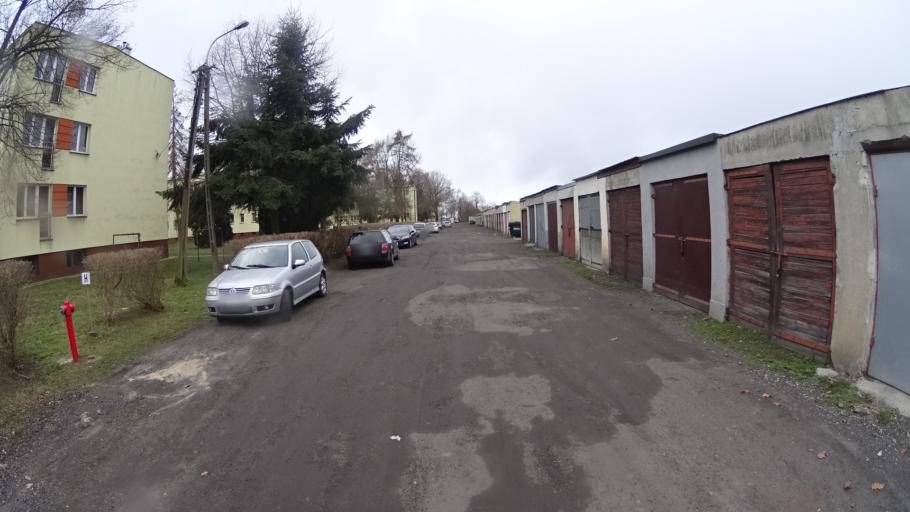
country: PL
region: Masovian Voivodeship
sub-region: Powiat warszawski zachodni
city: Blonie
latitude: 52.2169
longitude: 20.6455
